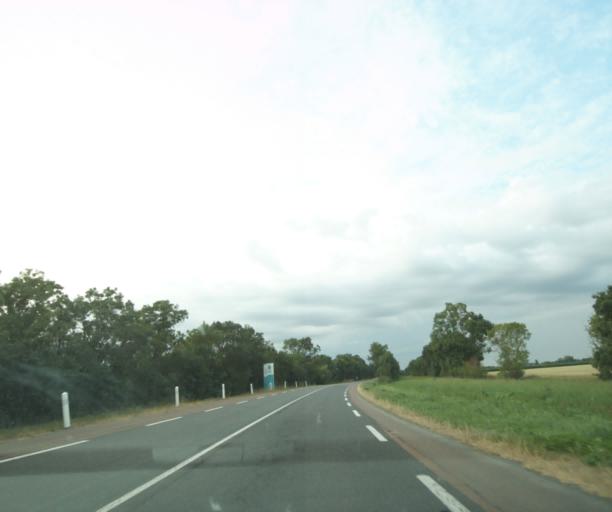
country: FR
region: Poitou-Charentes
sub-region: Departement de la Charente-Maritime
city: Marans
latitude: 46.3409
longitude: -0.9990
